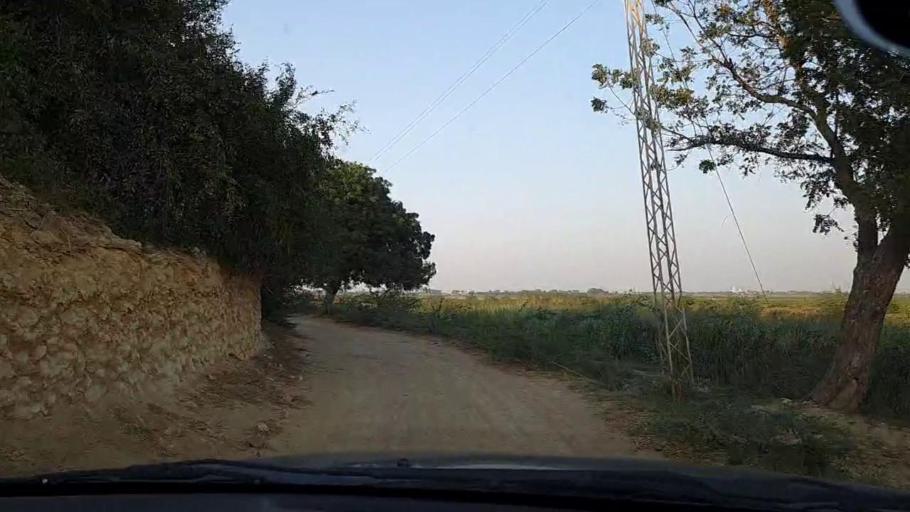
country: PK
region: Sindh
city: Thatta
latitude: 24.5620
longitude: 67.8802
